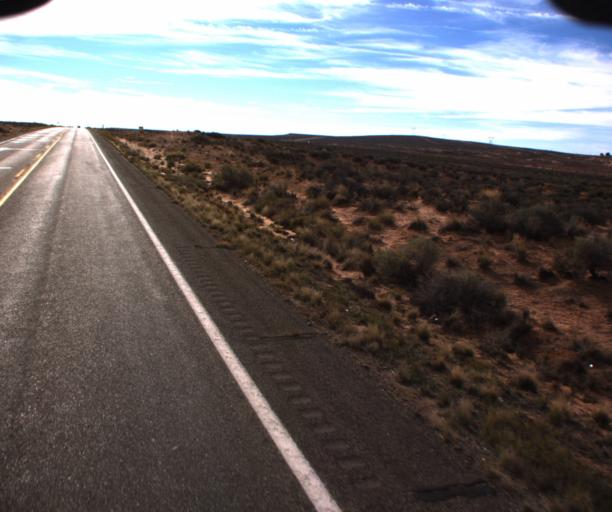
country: US
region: Arizona
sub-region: Coconino County
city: LeChee
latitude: 36.8321
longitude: -111.3152
